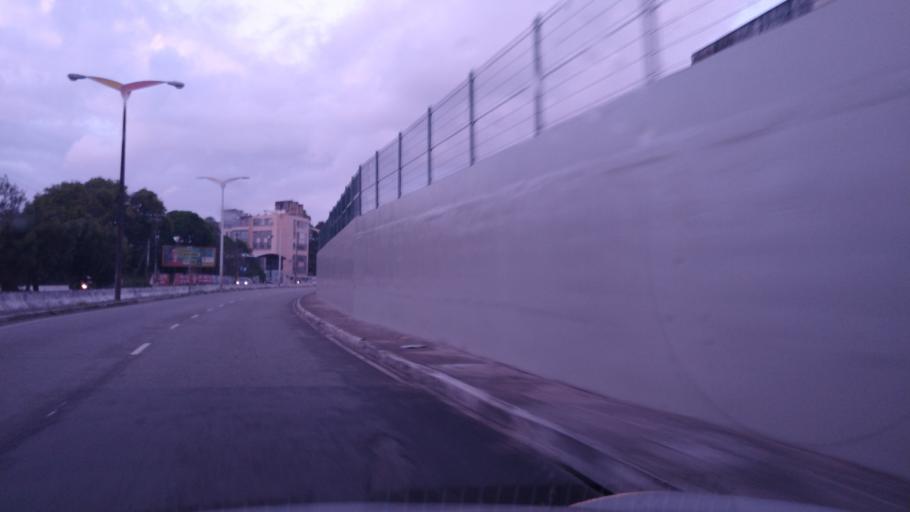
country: BR
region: Ceara
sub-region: Fortaleza
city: Fortaleza
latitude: -3.7503
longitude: -38.4947
